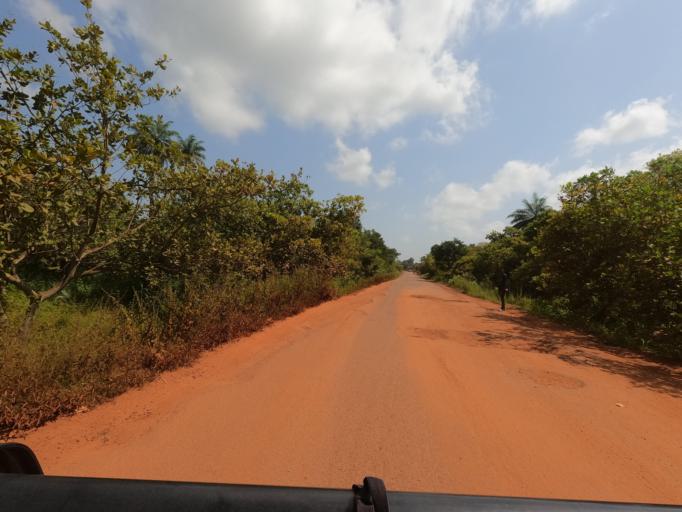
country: GW
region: Oio
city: Bissora
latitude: 12.2867
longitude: -15.7773
